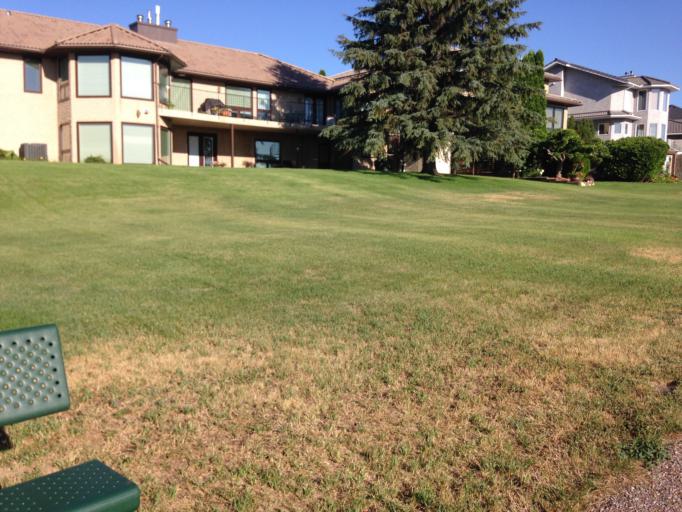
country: CA
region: Alberta
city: Medicine Hat
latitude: 49.9952
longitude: -110.6223
